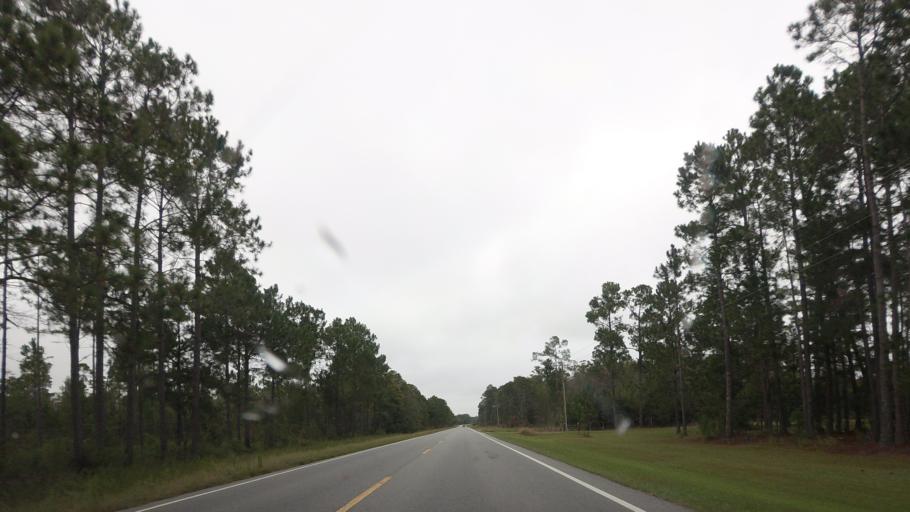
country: US
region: Georgia
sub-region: Berrien County
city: Nashville
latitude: 31.2766
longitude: -83.2395
